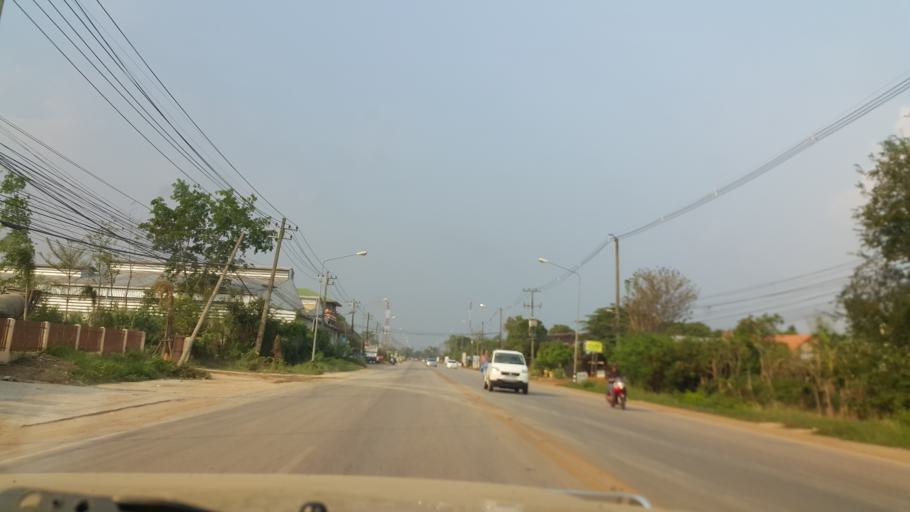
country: TH
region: Nakhon Phanom
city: That Phanom
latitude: 16.9492
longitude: 104.7216
